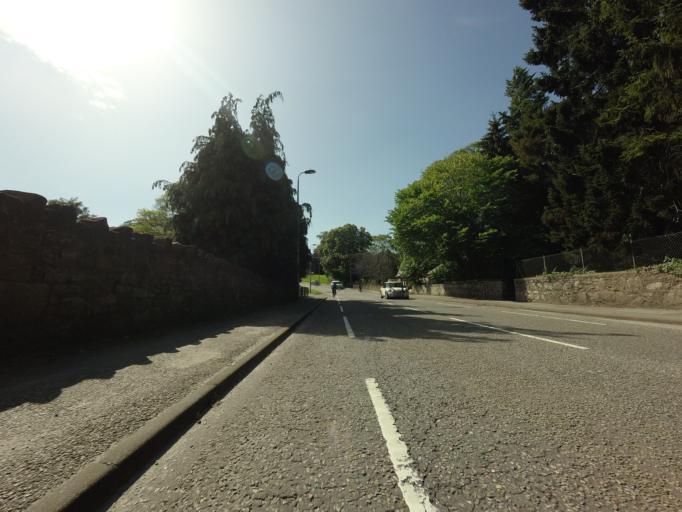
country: GB
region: Scotland
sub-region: Highland
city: Inverness
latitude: 57.4731
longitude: -4.2062
